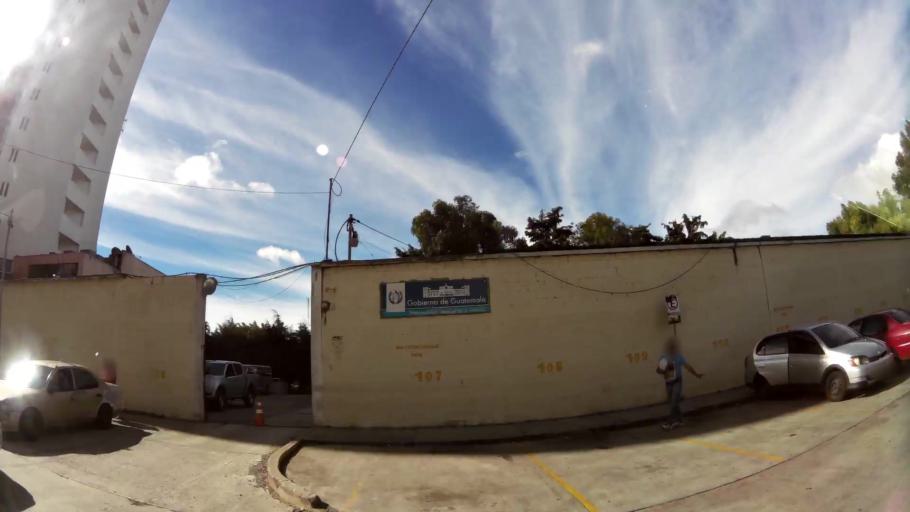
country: GT
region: Guatemala
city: Santa Catarina Pinula
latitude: 14.5880
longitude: -90.5213
